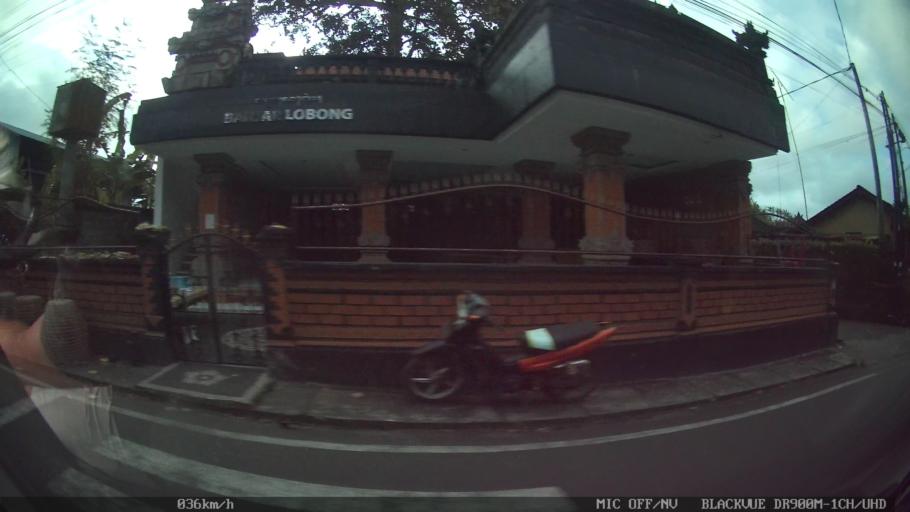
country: ID
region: Bali
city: Banjar Tebongkang
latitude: -8.5229
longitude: 115.2492
